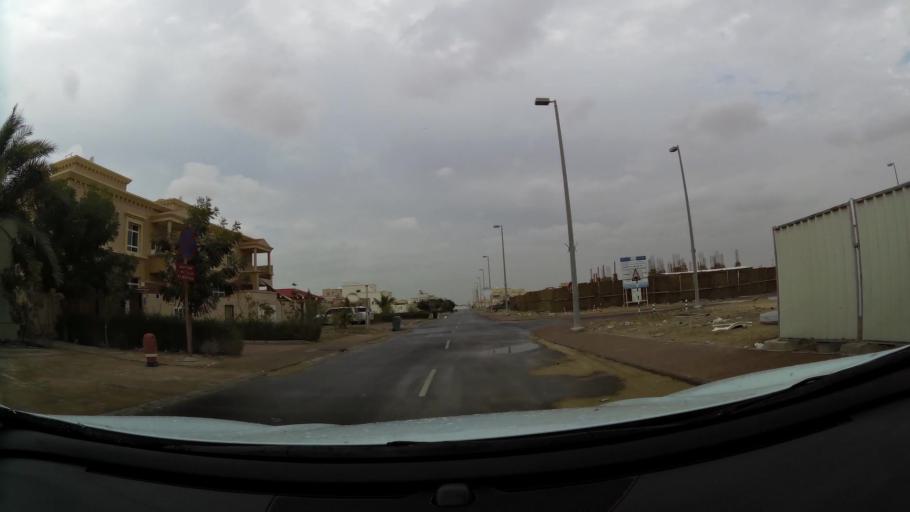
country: AE
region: Abu Dhabi
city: Abu Dhabi
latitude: 24.3569
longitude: 54.6227
